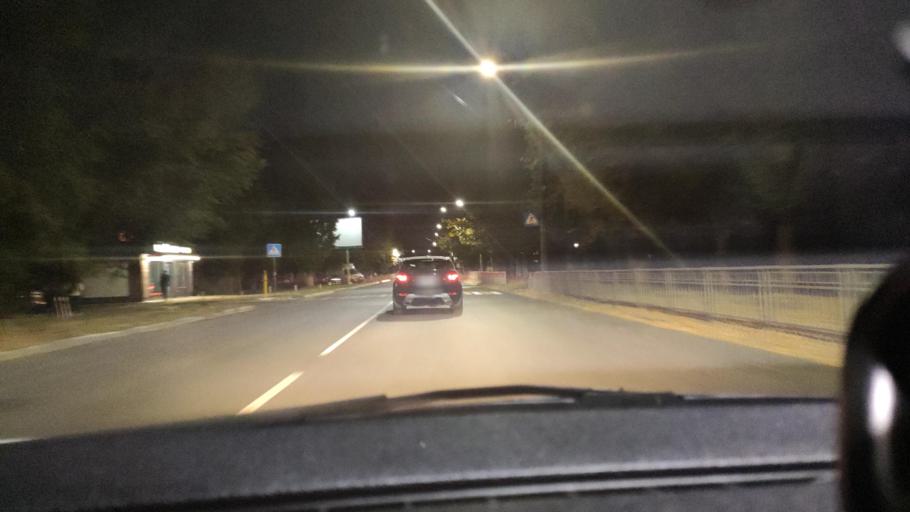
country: RU
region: Voronezj
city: Voronezh
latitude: 51.6805
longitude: 39.1920
